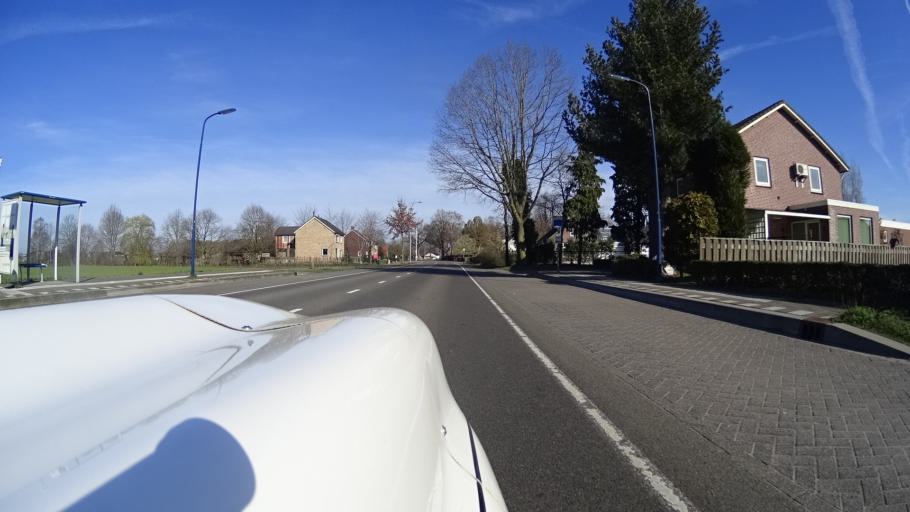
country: NL
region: North Brabant
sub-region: Gemeente Boekel
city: Boekel
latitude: 51.6139
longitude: 5.6700
